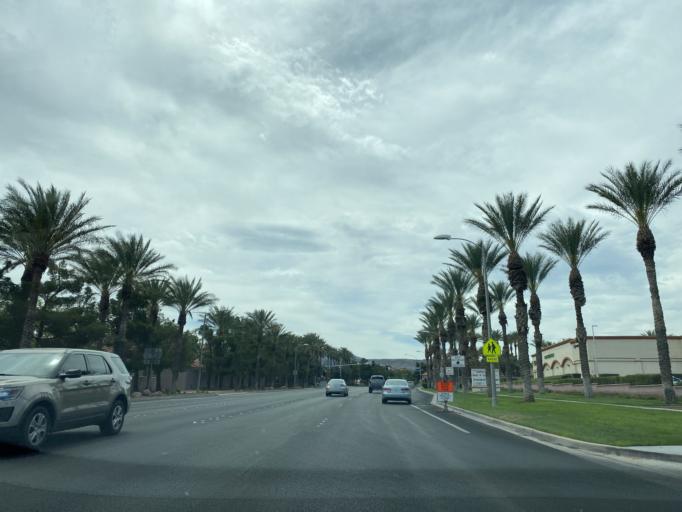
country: US
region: Nevada
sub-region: Clark County
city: Whitney
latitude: 36.0255
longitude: -115.0624
